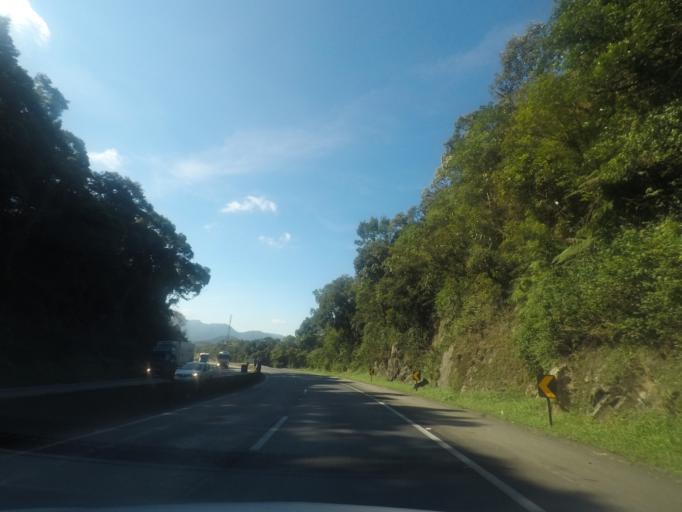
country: BR
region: Parana
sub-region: Piraquara
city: Piraquara
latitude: -25.5851
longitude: -48.9577
